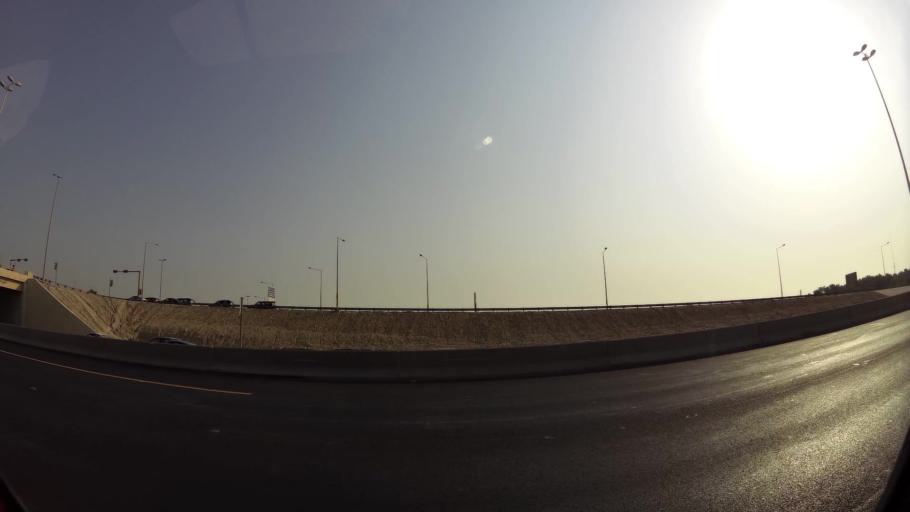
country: KW
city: Al Funaytis
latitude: 29.2481
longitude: 48.0918
